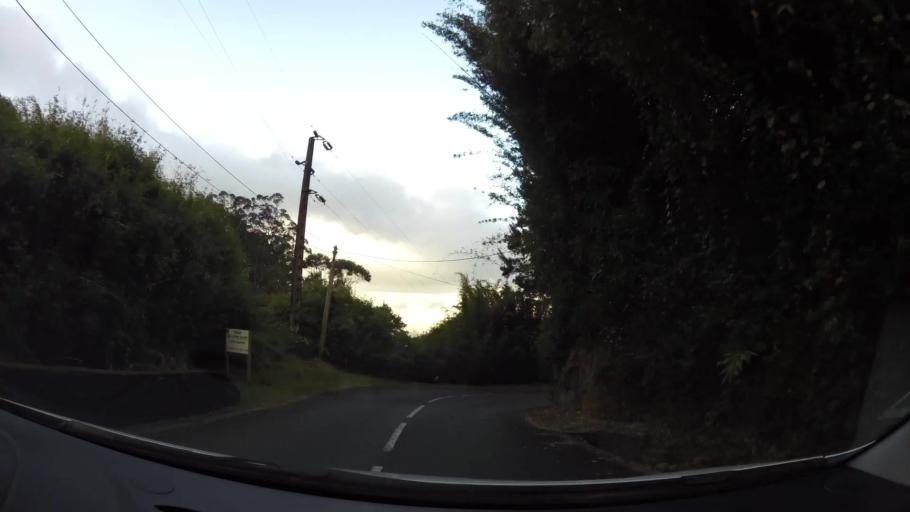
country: RE
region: Reunion
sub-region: Reunion
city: Saint-Denis
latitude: -20.9234
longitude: 55.4378
